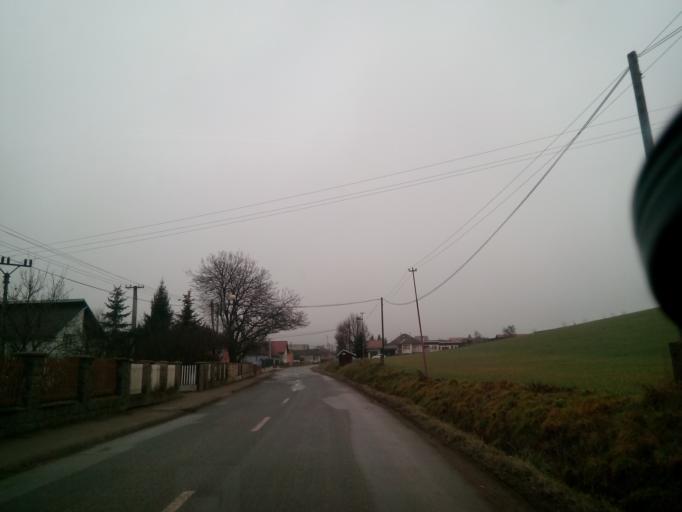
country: SK
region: Kosicky
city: Krompachy
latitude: 48.9738
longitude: 20.9497
